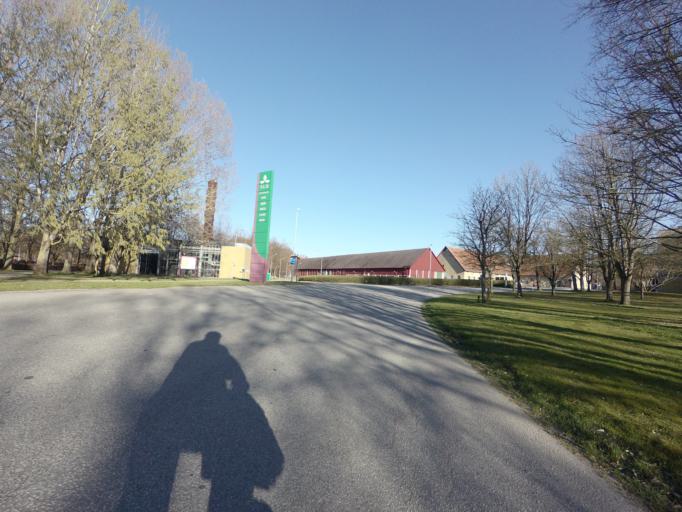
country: SE
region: Skane
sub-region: Lomma Kommun
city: Lomma
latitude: 55.6578
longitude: 13.0819
